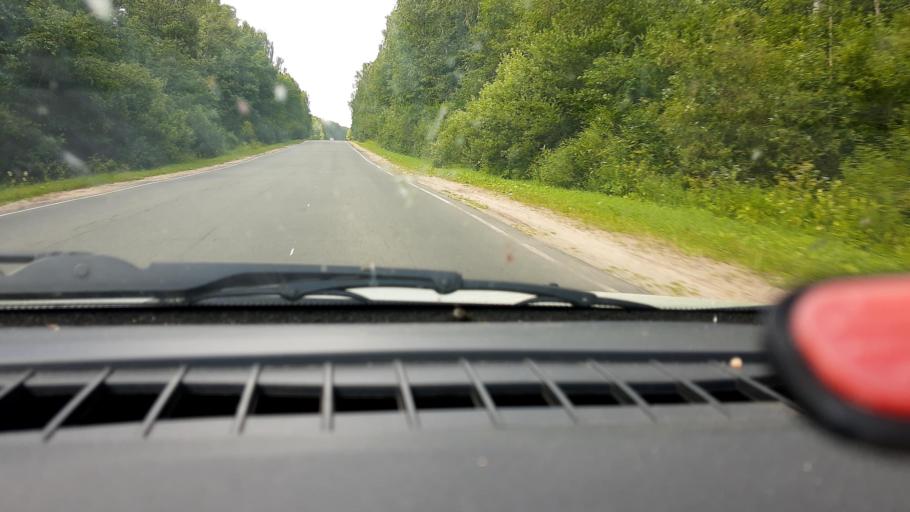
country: RU
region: Nizjnij Novgorod
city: Prudy
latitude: 57.4086
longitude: 46.0748
